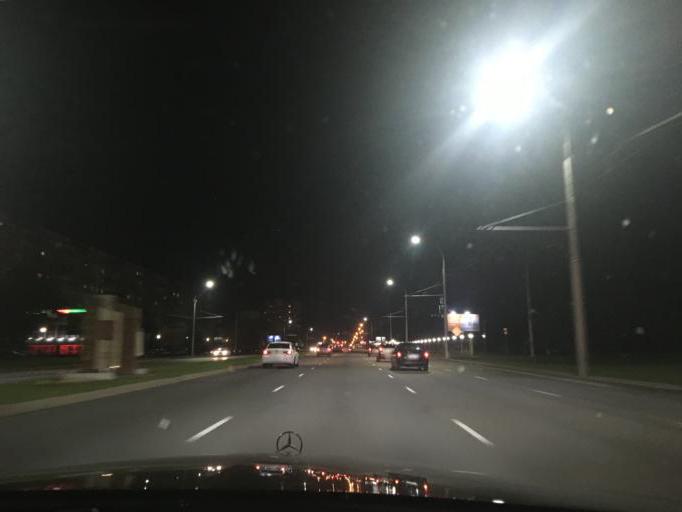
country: BY
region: Brest
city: Brest
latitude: 52.0975
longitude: 23.7538
